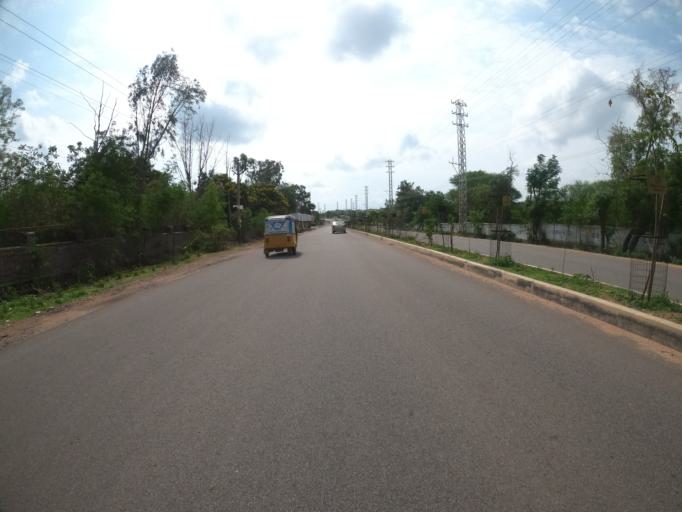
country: IN
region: Telangana
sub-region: Medak
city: Serilingampalle
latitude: 17.3932
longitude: 78.3209
